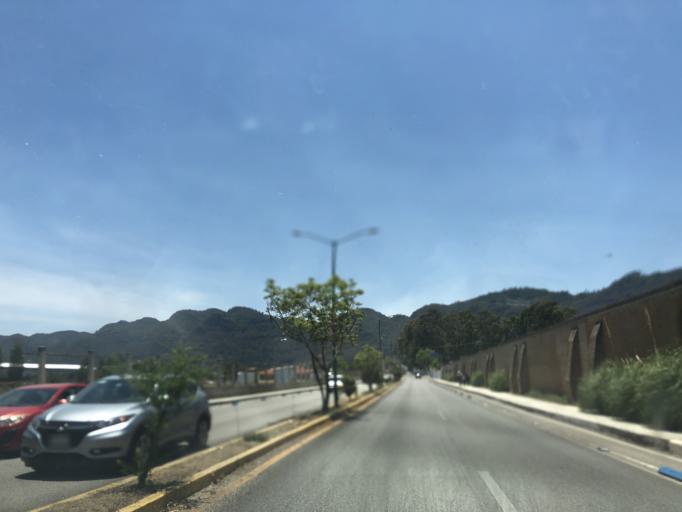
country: MX
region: Chiapas
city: San Cristobal de las Casas
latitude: 16.7284
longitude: -92.6512
